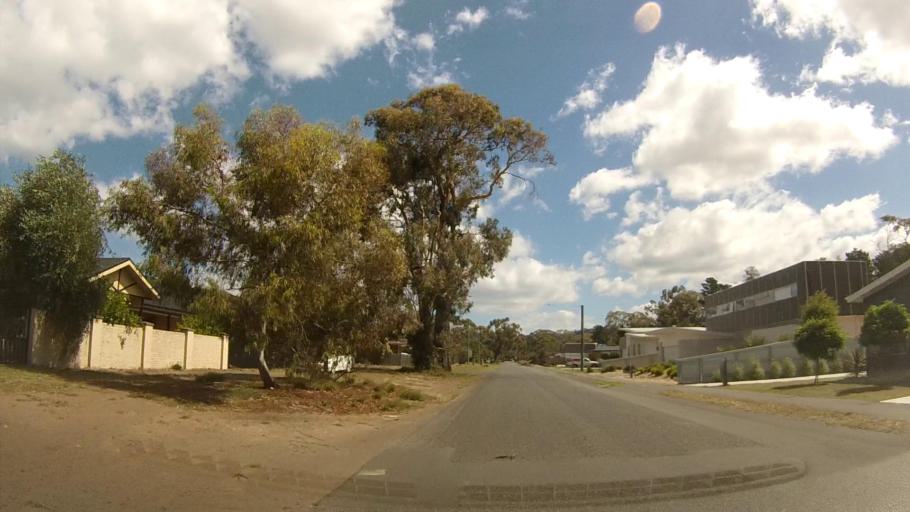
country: AU
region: Tasmania
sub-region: Clarence
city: Seven Mile Beach
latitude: -42.8552
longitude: 147.5054
